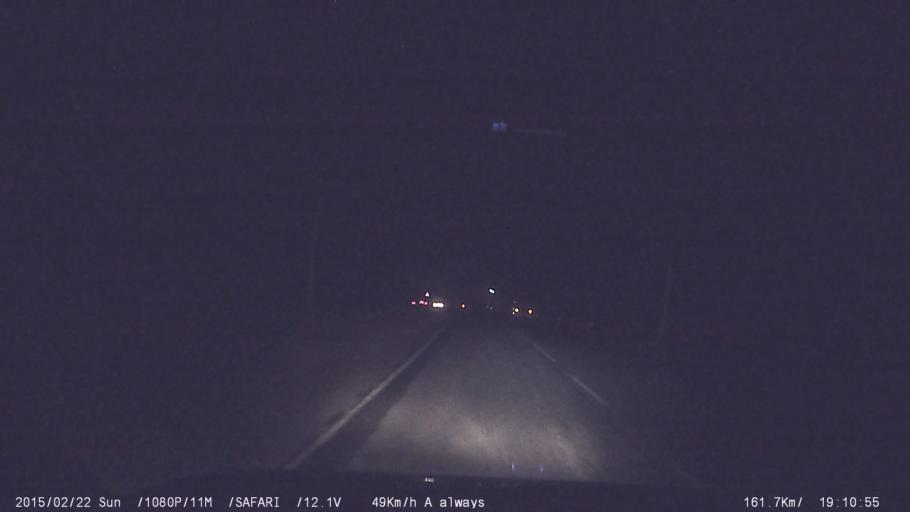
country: IN
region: Tamil Nadu
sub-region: Theni
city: Teni
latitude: 10.0646
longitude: 77.5126
